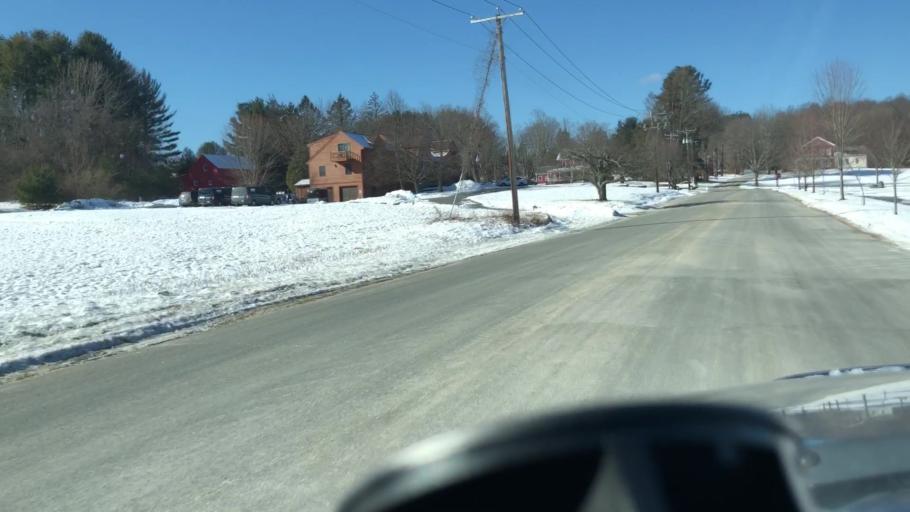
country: US
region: Massachusetts
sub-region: Hampshire County
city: Southampton
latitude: 42.2244
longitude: -72.7293
